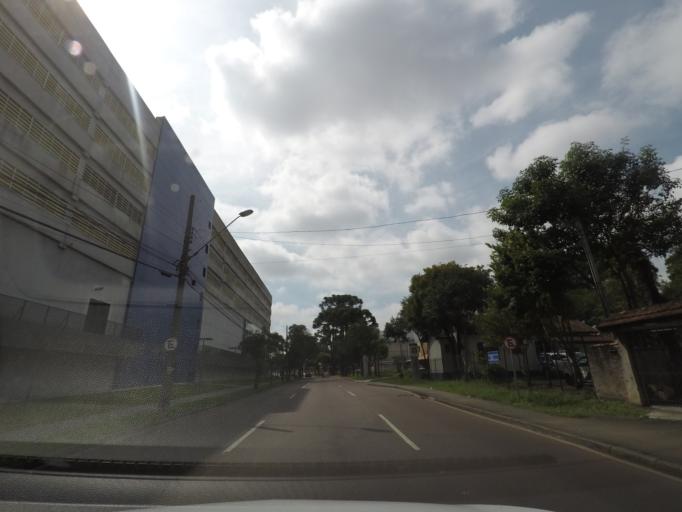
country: BR
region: Parana
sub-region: Curitiba
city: Curitiba
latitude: -25.4792
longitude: -49.2941
